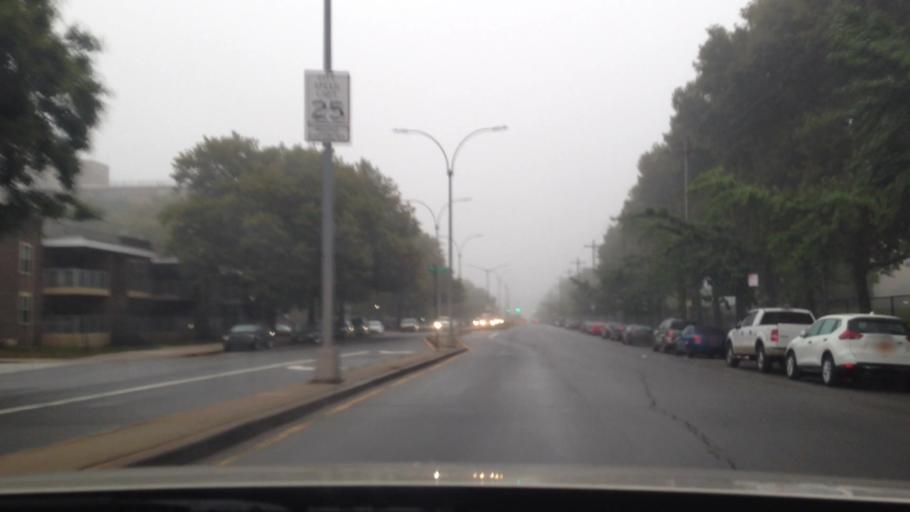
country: US
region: New York
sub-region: Kings County
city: East New York
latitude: 40.6529
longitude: -73.8859
